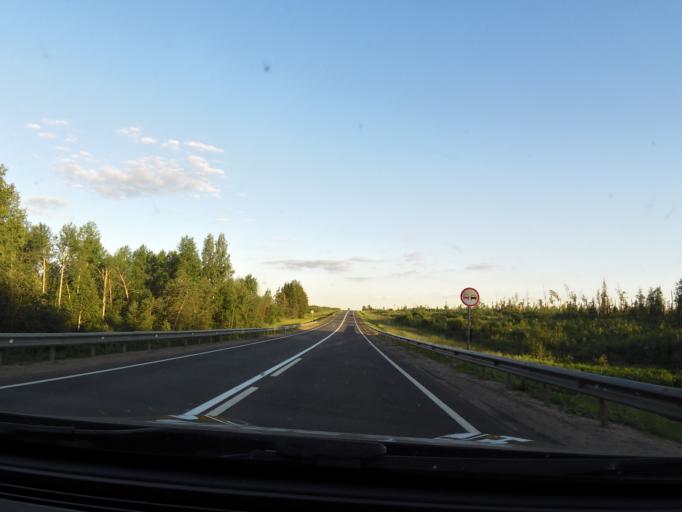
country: RU
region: Jaroslavl
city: Prechistoye
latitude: 58.5966
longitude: 40.3432
